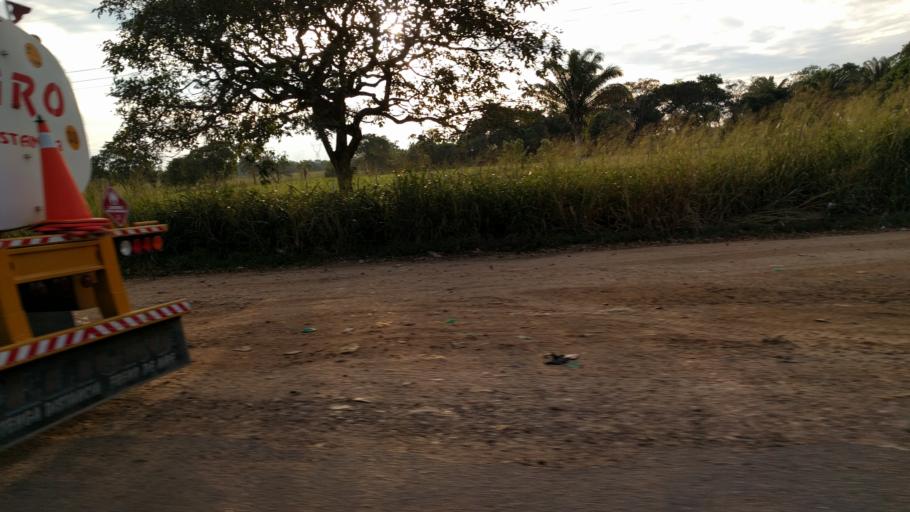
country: BO
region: Santa Cruz
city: Buena Vista
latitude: -17.4237
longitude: -63.6259
